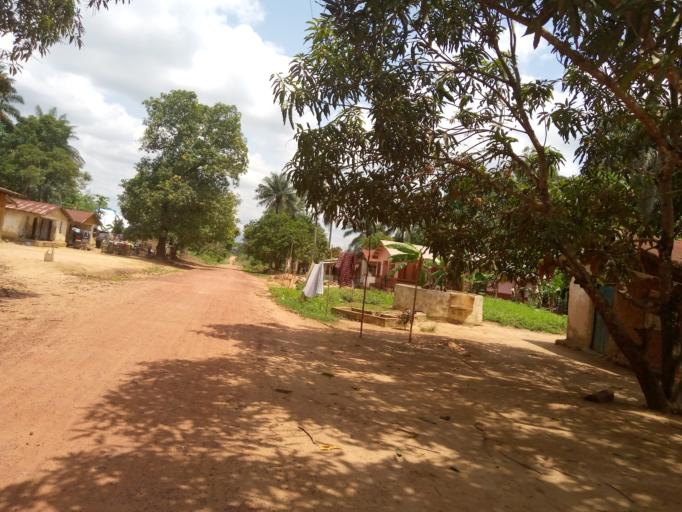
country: SL
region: Western Area
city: Waterloo
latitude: 8.3794
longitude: -12.9720
